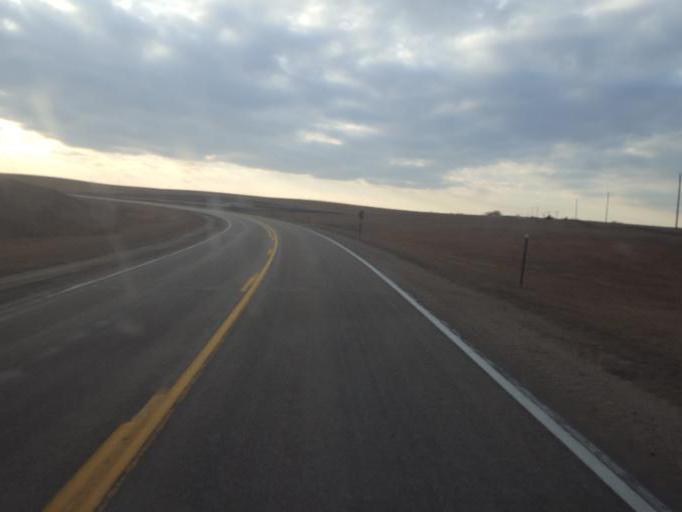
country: US
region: Nebraska
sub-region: Knox County
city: Bloomfield
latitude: 42.6125
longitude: -97.5201
